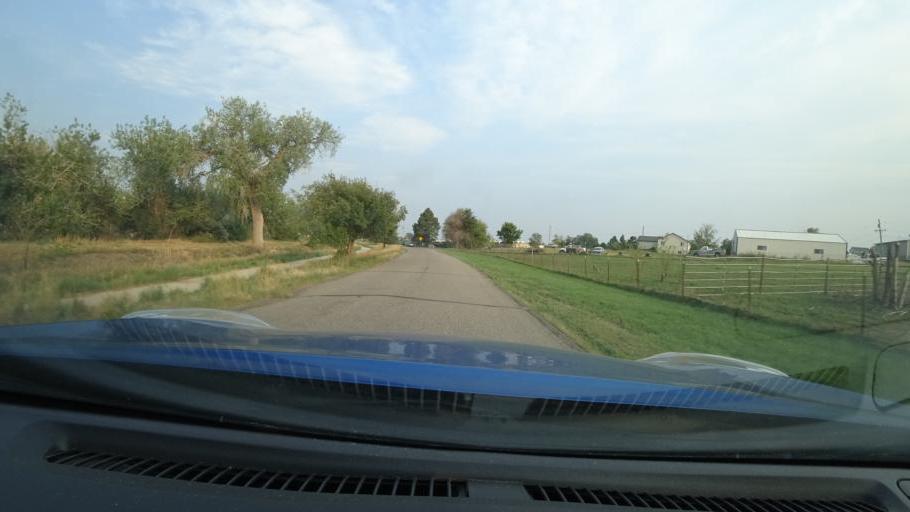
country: US
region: Colorado
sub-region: Adams County
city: Aurora
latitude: 39.7380
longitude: -104.7850
